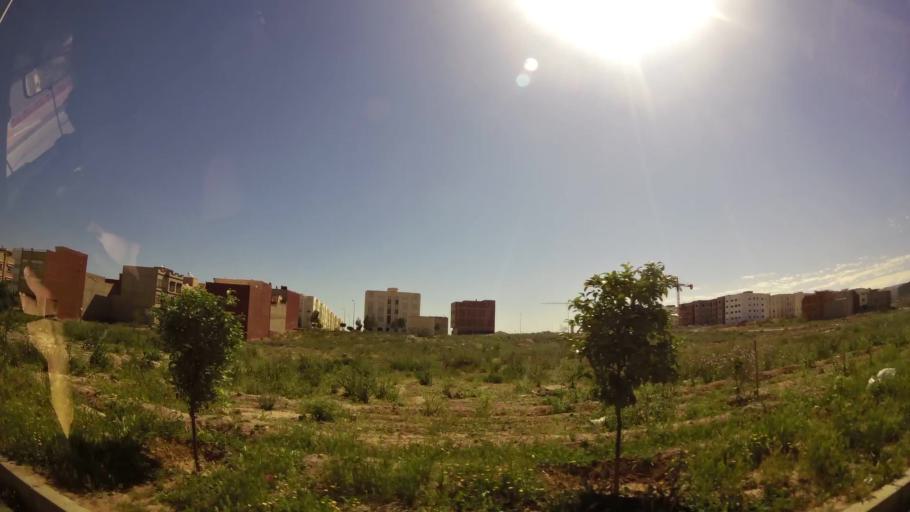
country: MA
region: Oriental
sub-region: Oujda-Angad
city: Oujda
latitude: 34.6547
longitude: -1.8848
